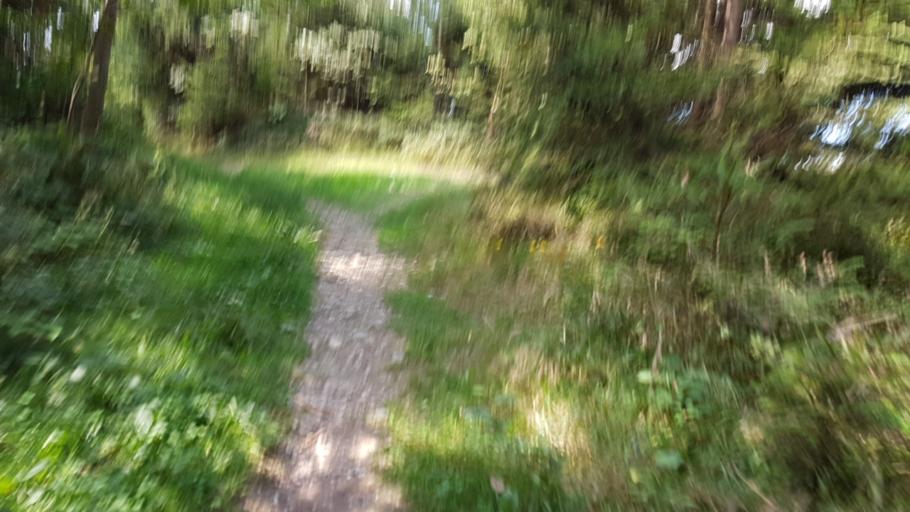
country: CH
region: Bern
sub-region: Thun District
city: Buchholterberg
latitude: 46.8282
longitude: 7.6714
